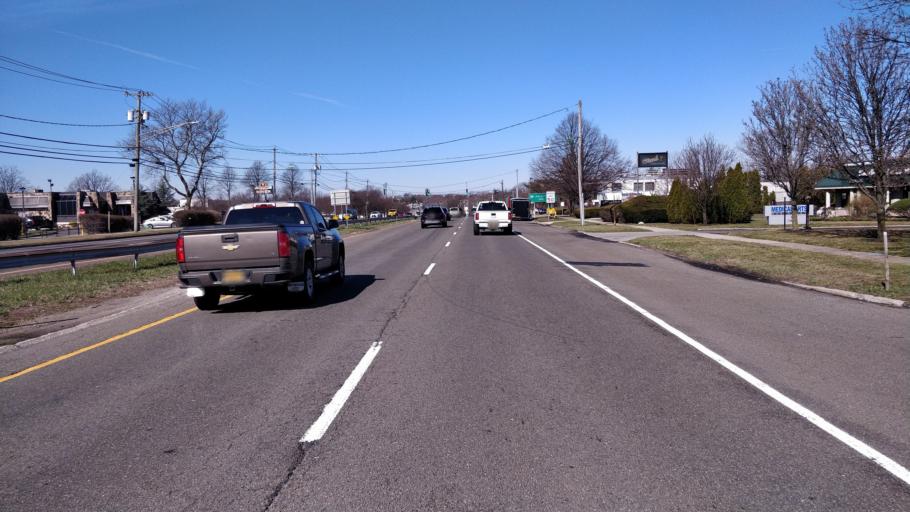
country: US
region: New York
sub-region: Suffolk County
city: Commack
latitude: 40.8411
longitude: -73.2856
